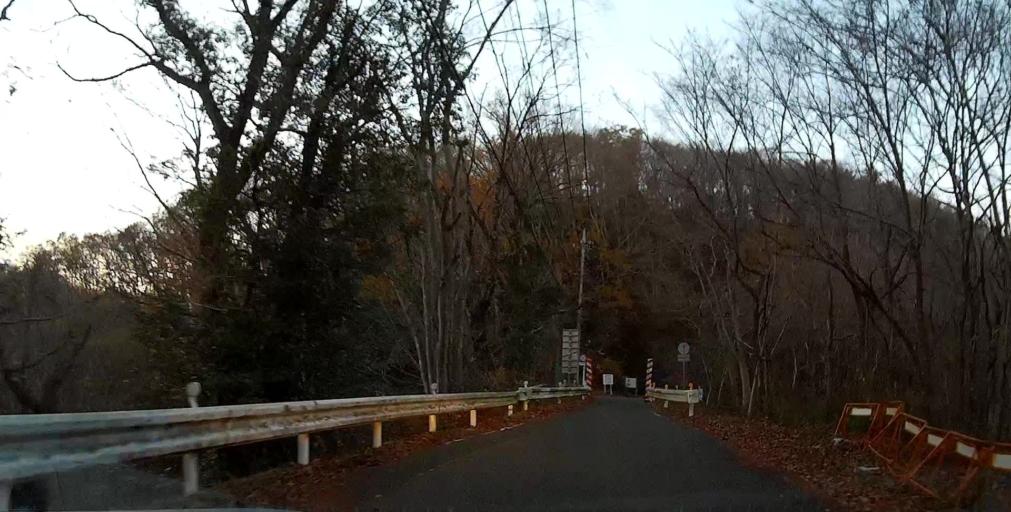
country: JP
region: Yamanashi
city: Uenohara
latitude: 35.5774
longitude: 139.1813
